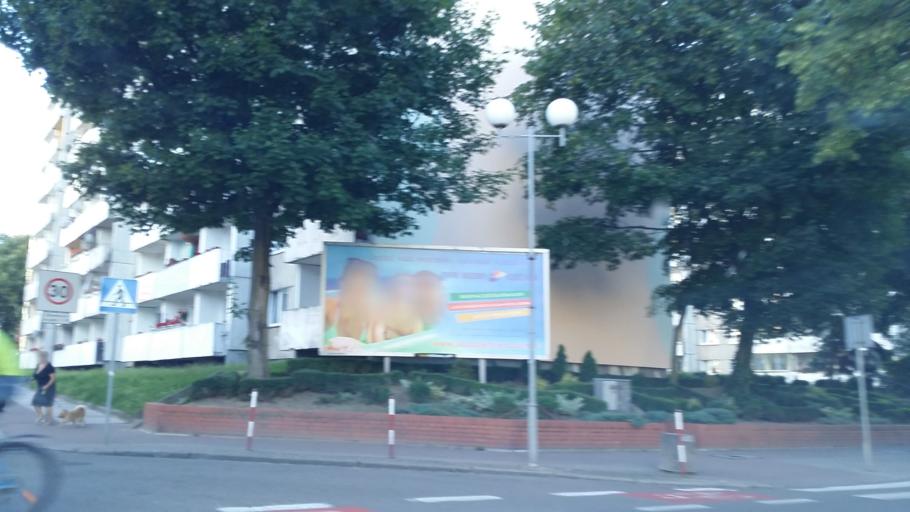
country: PL
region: West Pomeranian Voivodeship
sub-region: Powiat kolobrzeski
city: Kolobrzeg
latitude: 54.1776
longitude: 15.5793
